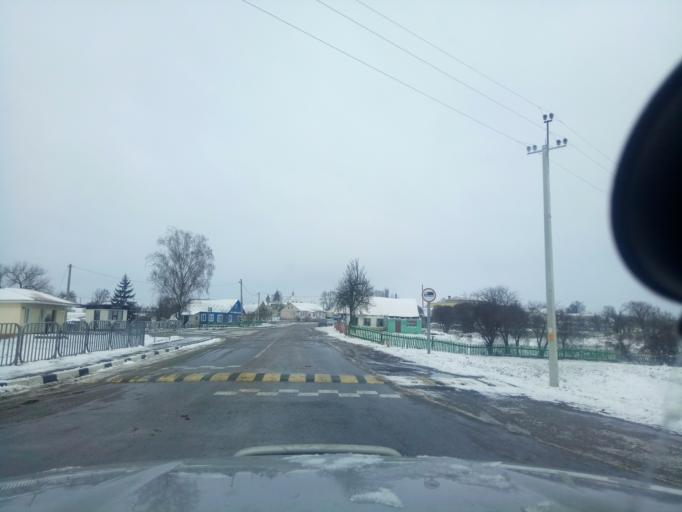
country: BY
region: Minsk
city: Tsimkavichy
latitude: 53.0698
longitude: 26.9896
